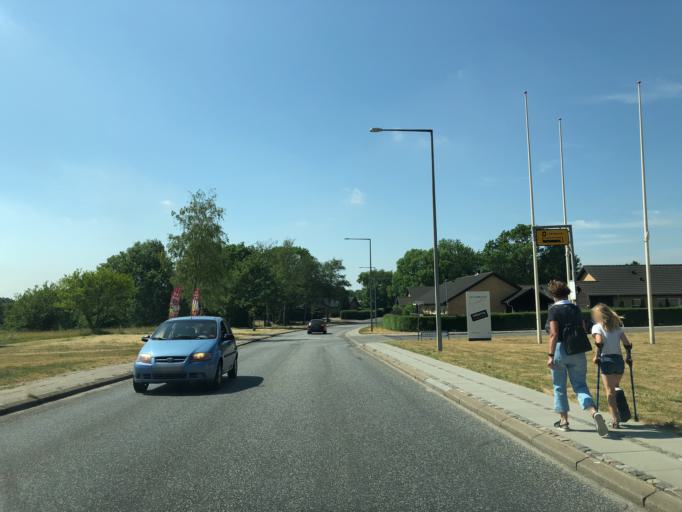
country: DK
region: South Denmark
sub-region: Kolding Kommune
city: Kolding
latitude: 55.5204
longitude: 9.4776
